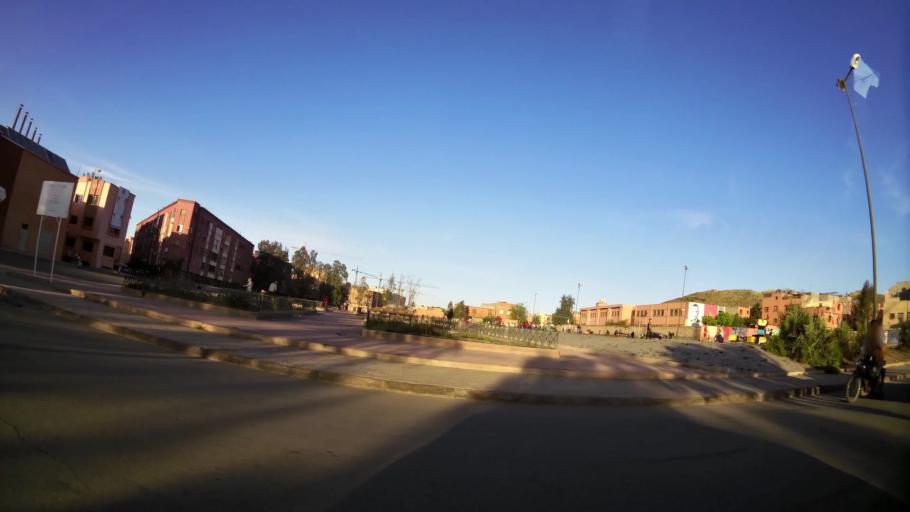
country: MA
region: Marrakech-Tensift-Al Haouz
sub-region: Marrakech
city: Marrakesh
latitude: 31.6531
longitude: -8.0320
